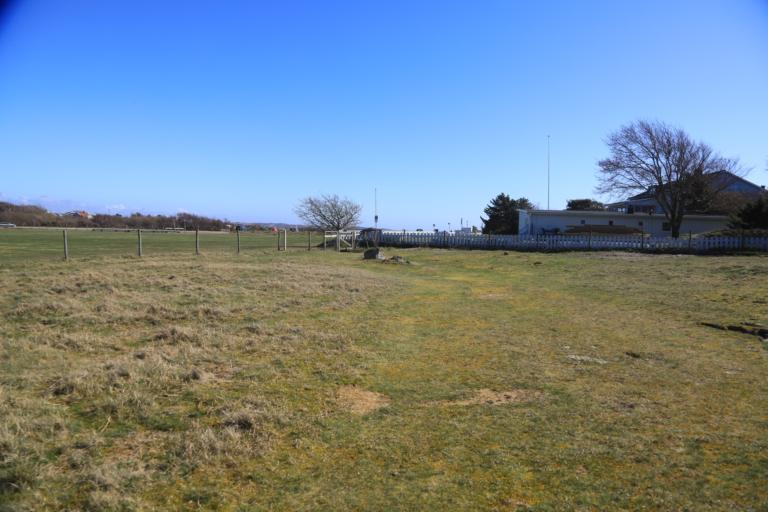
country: SE
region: Halland
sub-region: Varbergs Kommun
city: Varberg
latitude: 57.1203
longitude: 12.1995
